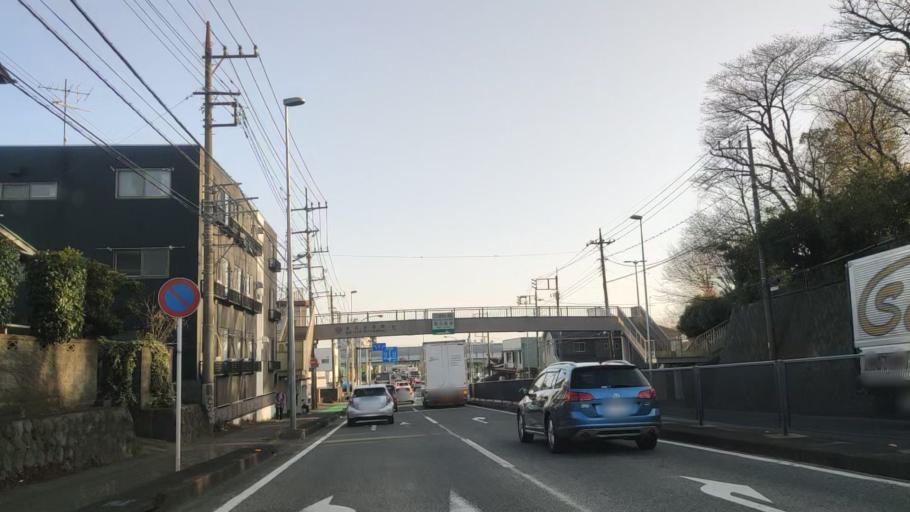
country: JP
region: Kanagawa
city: Atsugi
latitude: 35.4668
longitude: 139.3683
